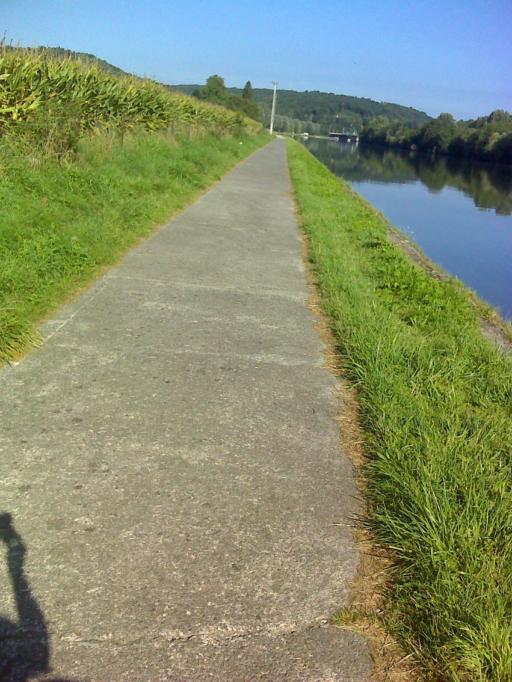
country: BE
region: Wallonia
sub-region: Province de Namur
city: Anhee
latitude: 50.3068
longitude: 4.8889
